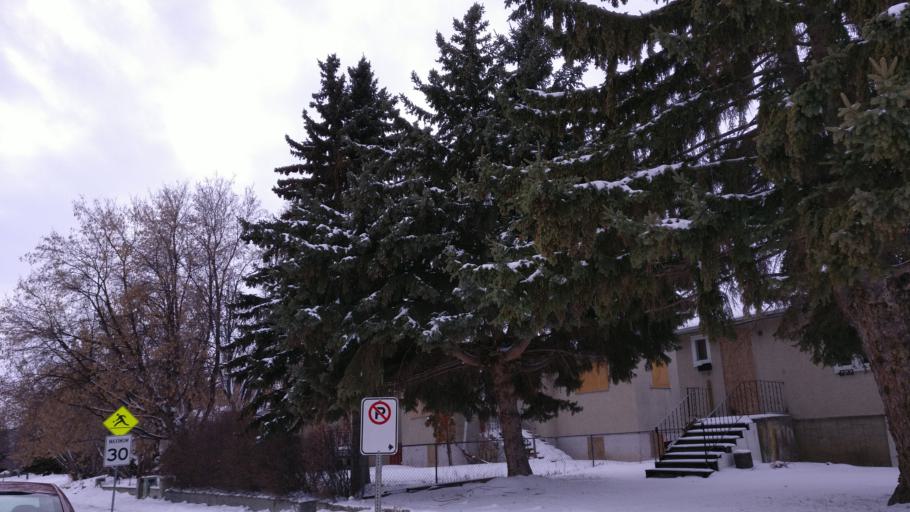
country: CA
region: Alberta
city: Red Deer
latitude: 52.2670
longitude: -113.8075
